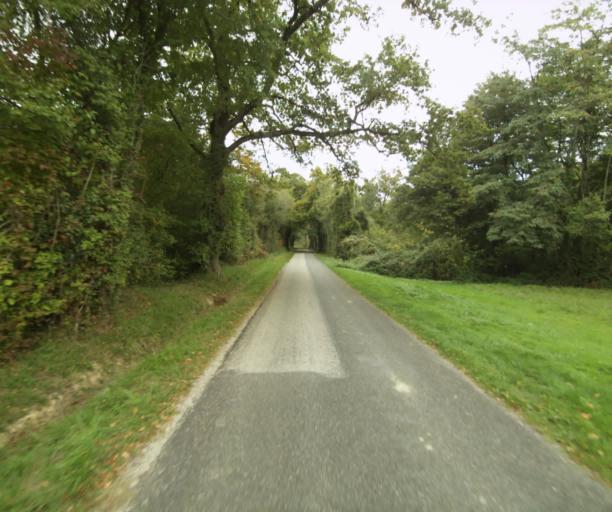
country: FR
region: Midi-Pyrenees
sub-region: Departement du Gers
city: Eauze
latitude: 43.8907
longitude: 0.1278
